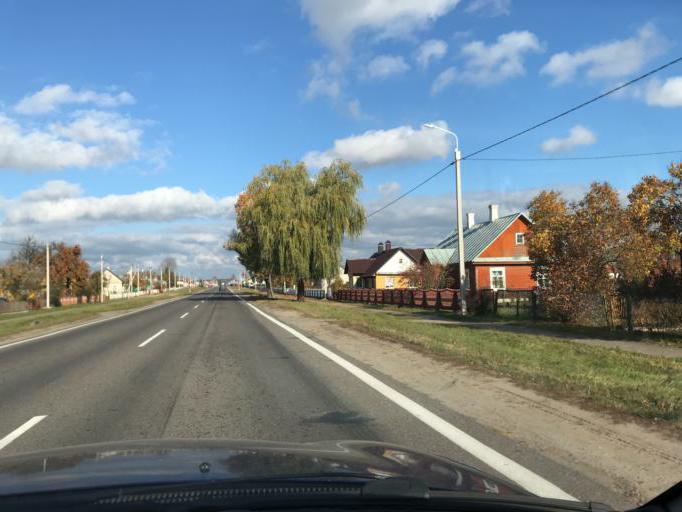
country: LT
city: Salcininkai
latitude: 54.2460
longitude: 25.3555
